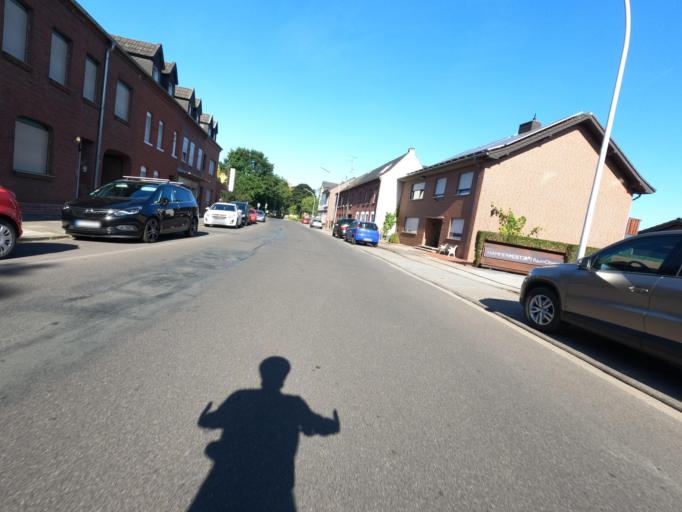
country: DE
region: North Rhine-Westphalia
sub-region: Regierungsbezirk Koln
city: Wassenberg
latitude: 51.0597
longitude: 6.1491
